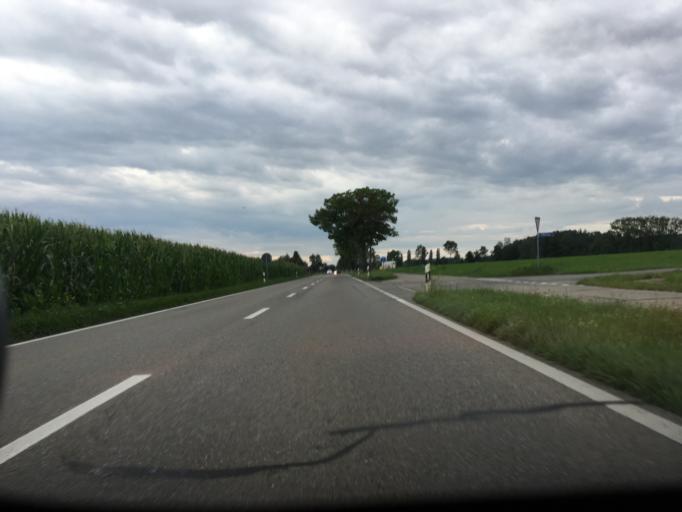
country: CH
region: Zurich
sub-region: Bezirk Pfaeffikon
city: Pfaeffikon / Pfaeffikon (Dorfkern)
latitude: 47.3762
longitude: 8.7689
